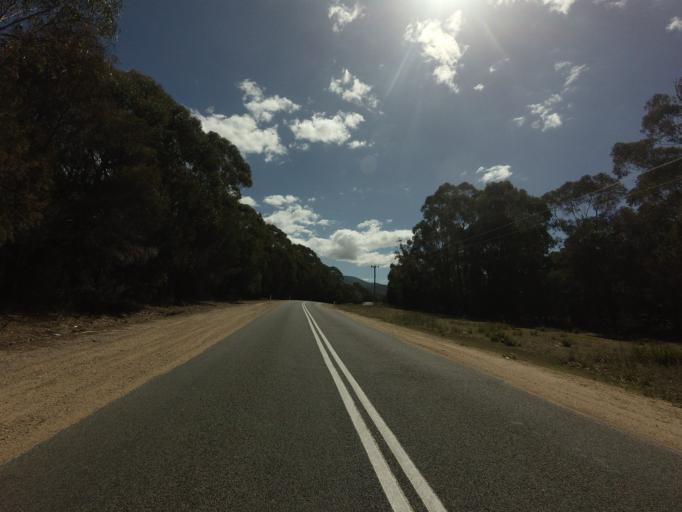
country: AU
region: Tasmania
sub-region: Break O'Day
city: St Helens
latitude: -41.6809
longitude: 148.2796
